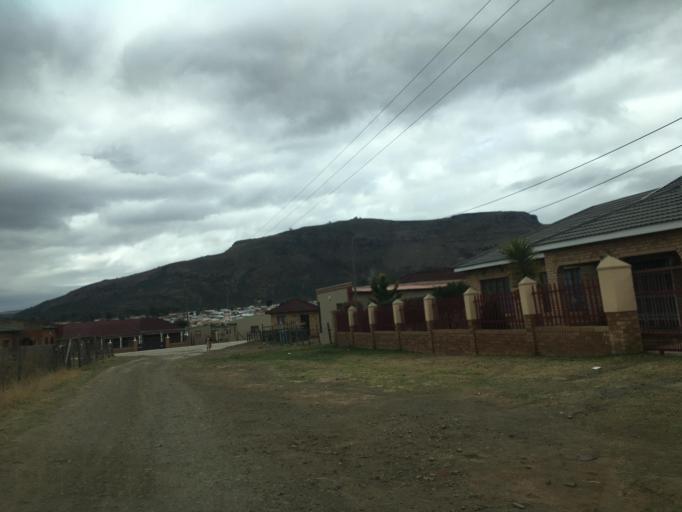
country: ZA
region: Eastern Cape
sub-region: Chris Hani District Municipality
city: Cala
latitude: -31.5379
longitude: 27.6972
